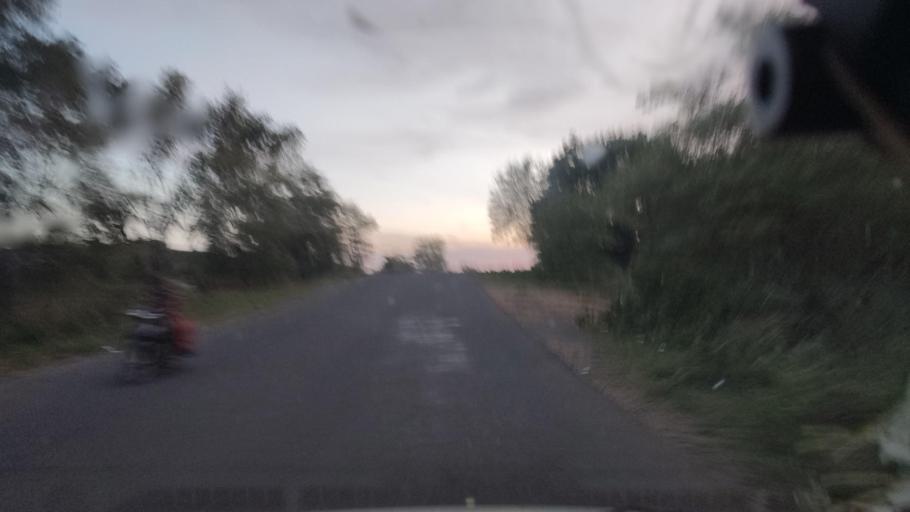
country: MM
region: Magway
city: Magway
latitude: 20.1696
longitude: 94.9265
